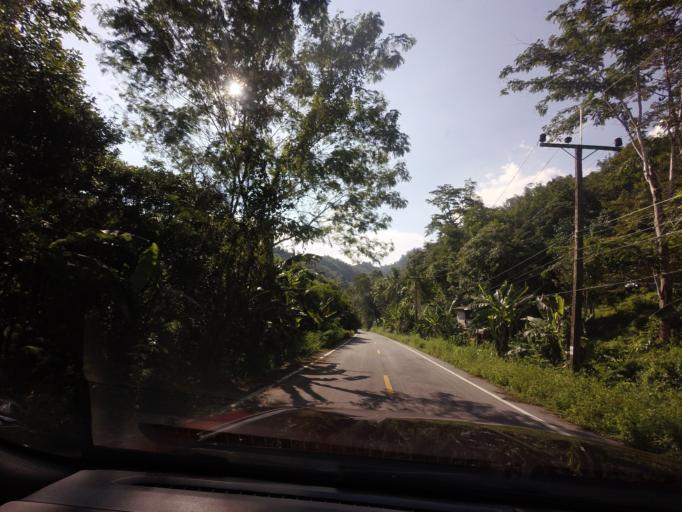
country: TH
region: Yala
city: Than To
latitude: 6.0742
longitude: 101.3396
